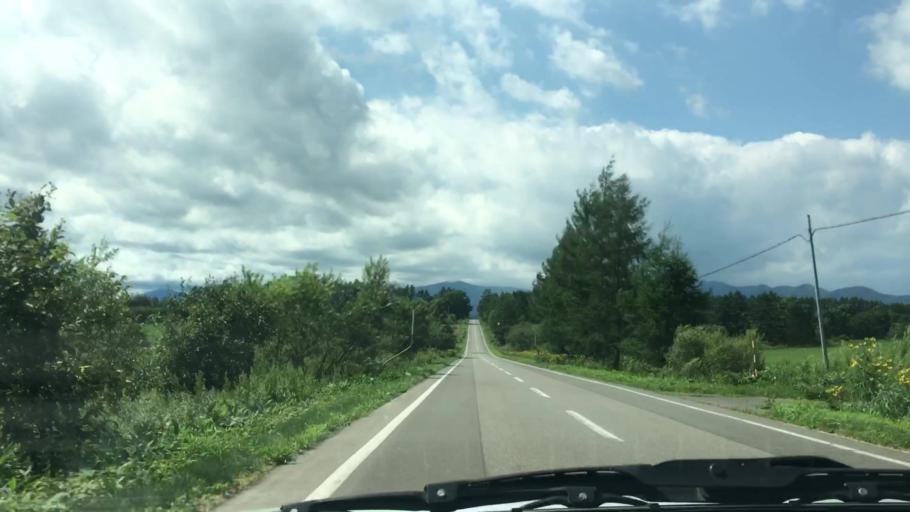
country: JP
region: Hokkaido
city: Otofuke
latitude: 43.2778
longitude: 143.3602
